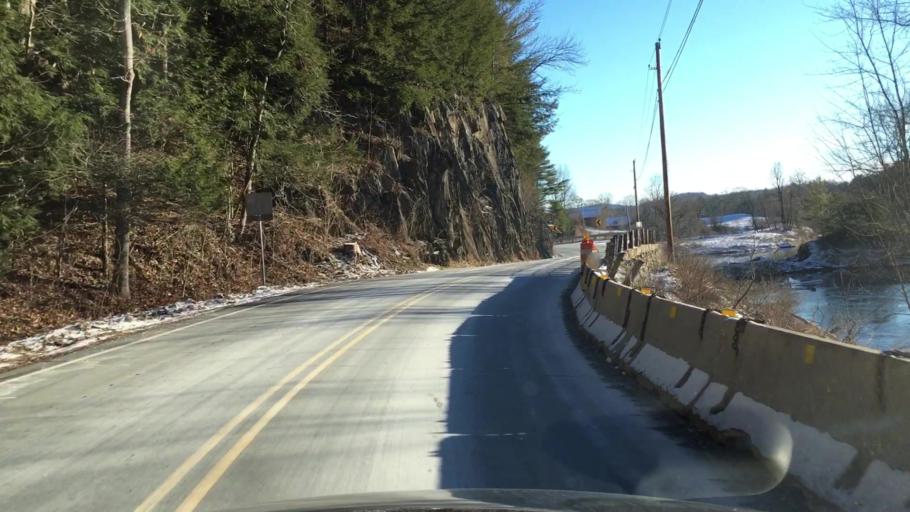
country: US
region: New Hampshire
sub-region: Grafton County
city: Woodsville
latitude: 44.1631
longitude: -72.0411
